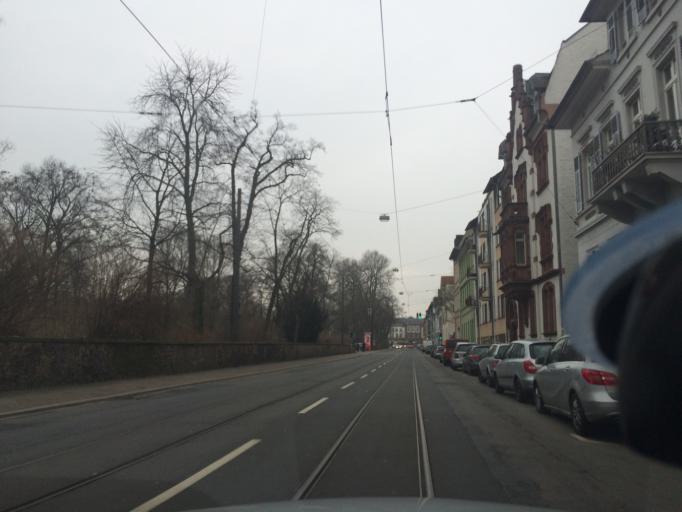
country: DE
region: Hesse
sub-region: Regierungsbezirk Darmstadt
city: Darmstadt
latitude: 49.8796
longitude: 8.6506
